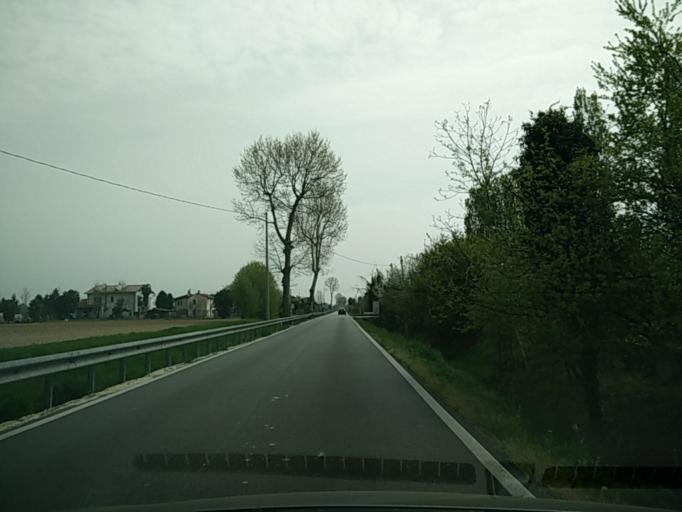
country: IT
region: Veneto
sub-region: Provincia di Venezia
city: Caltana
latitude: 45.4764
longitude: 12.0450
